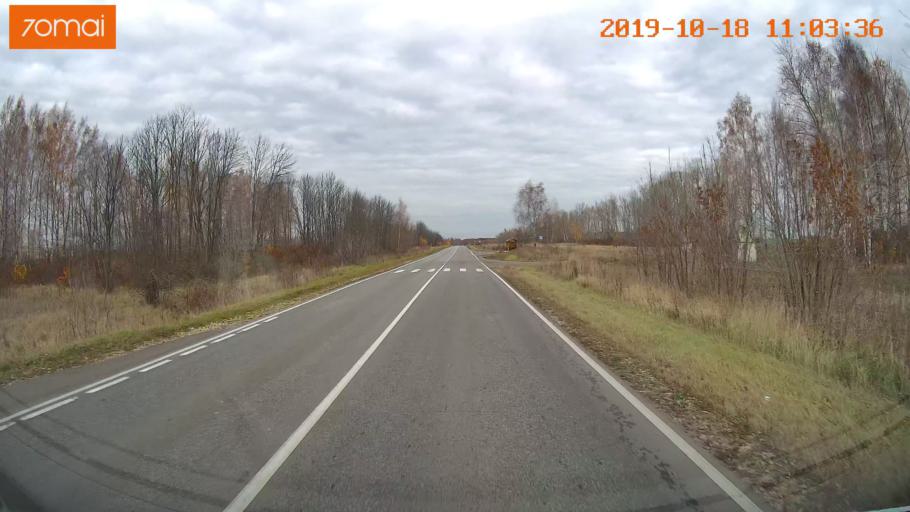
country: RU
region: Tula
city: Yepifan'
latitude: 53.8823
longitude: 38.5490
